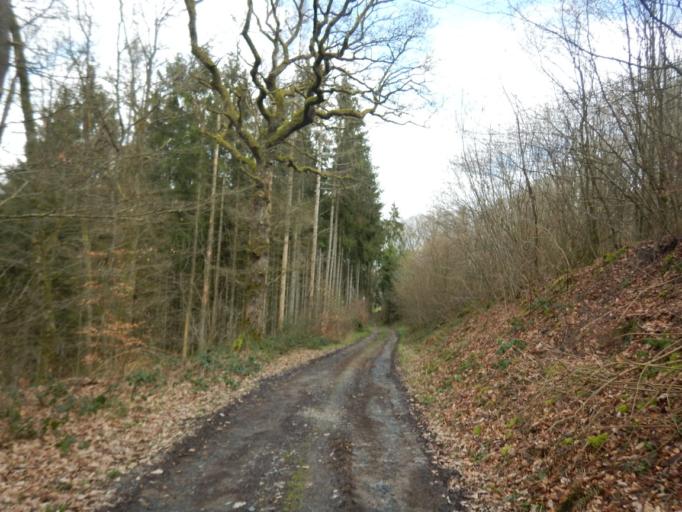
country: LU
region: Diekirch
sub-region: Canton de Wiltz
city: Esch-sur-Sure
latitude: 49.9226
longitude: 5.8967
